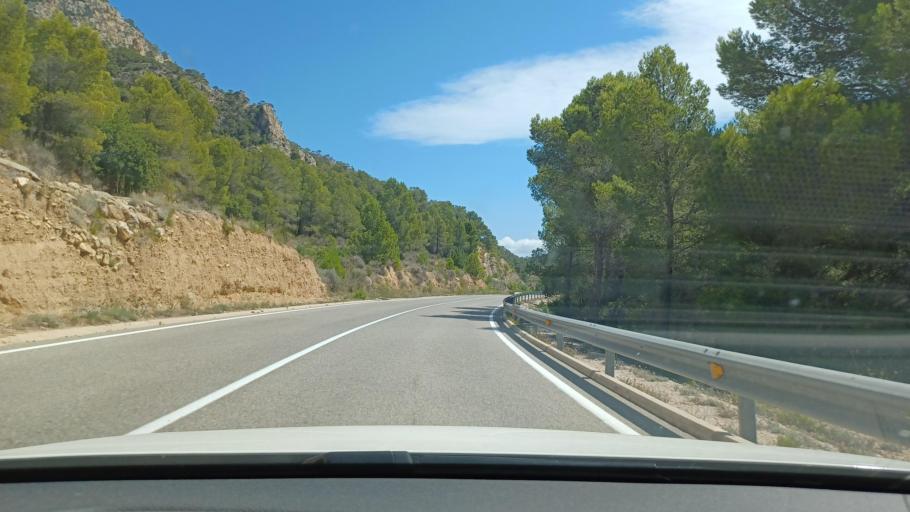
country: ES
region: Catalonia
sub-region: Provincia de Tarragona
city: Bot
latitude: 40.9757
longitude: 0.4226
